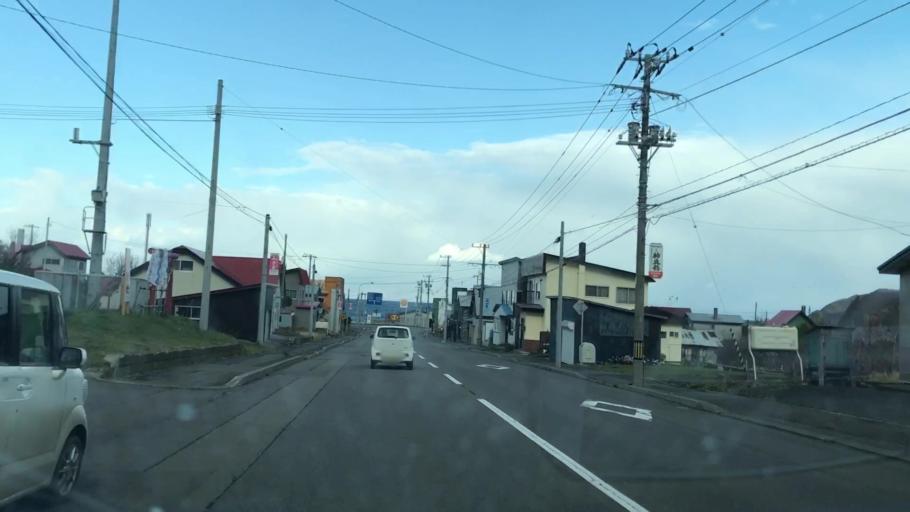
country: JP
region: Hokkaido
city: Yoichi
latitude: 43.3411
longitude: 140.4581
